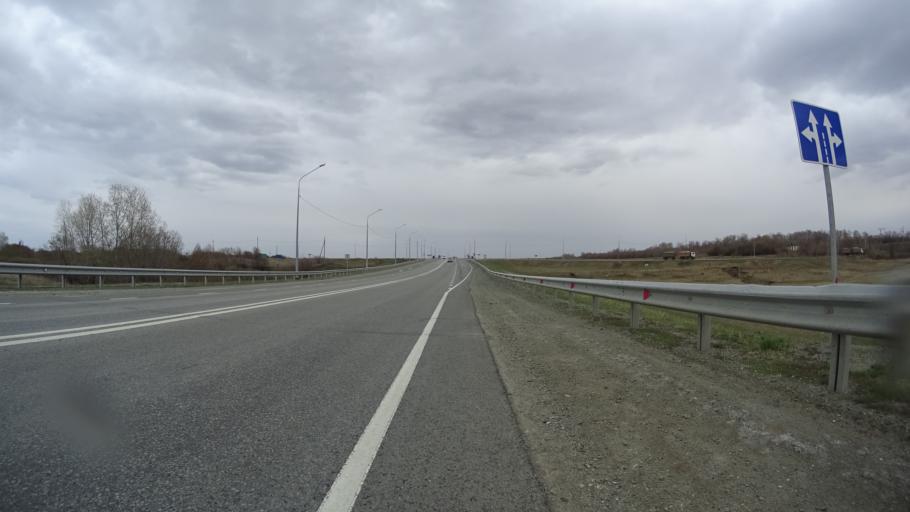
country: RU
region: Chelyabinsk
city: Krasnogorskiy
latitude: 54.6756
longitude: 61.2484
